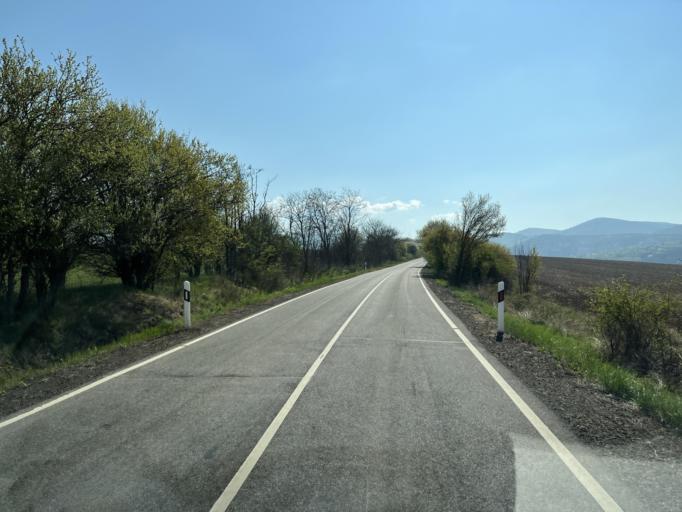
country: HU
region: Pest
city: Szob
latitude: 47.9384
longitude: 18.7884
